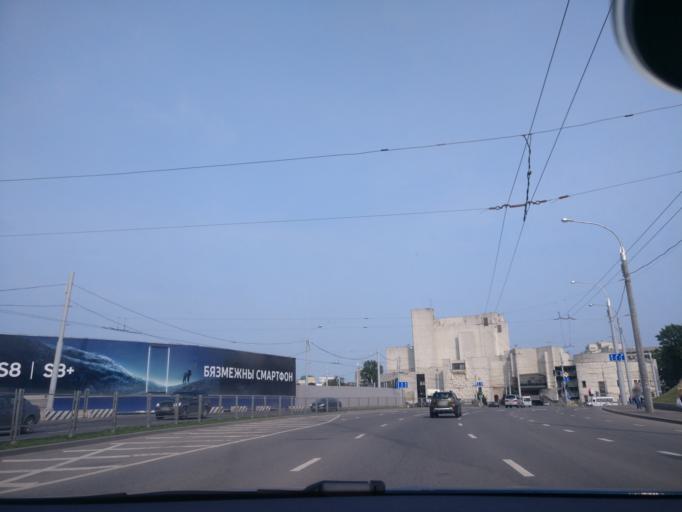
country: BY
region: Minsk
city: Minsk
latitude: 53.8955
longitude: 27.5367
